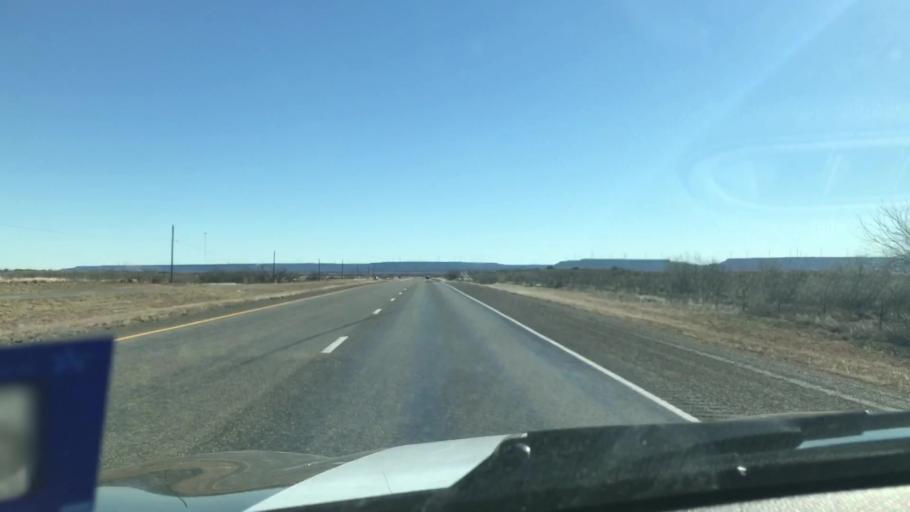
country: US
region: Texas
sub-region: Garza County
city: Post
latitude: 33.0839
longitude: -101.2415
